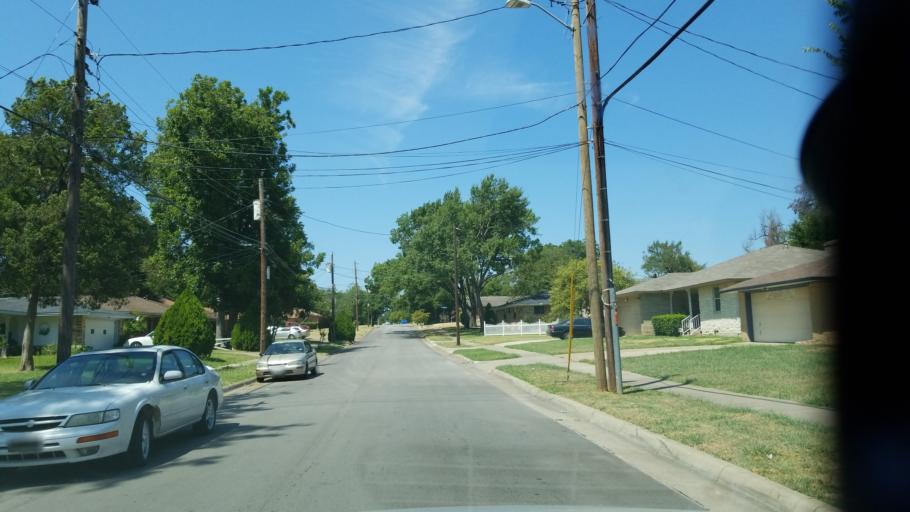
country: US
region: Texas
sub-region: Dallas County
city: Duncanville
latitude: 32.6526
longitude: -96.9001
